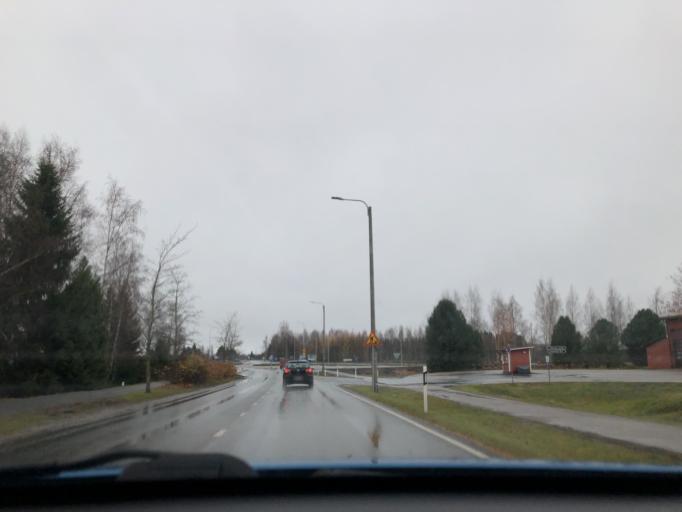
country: FI
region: Pirkanmaa
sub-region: Tampere
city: Kangasala
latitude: 61.4668
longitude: 24.0385
